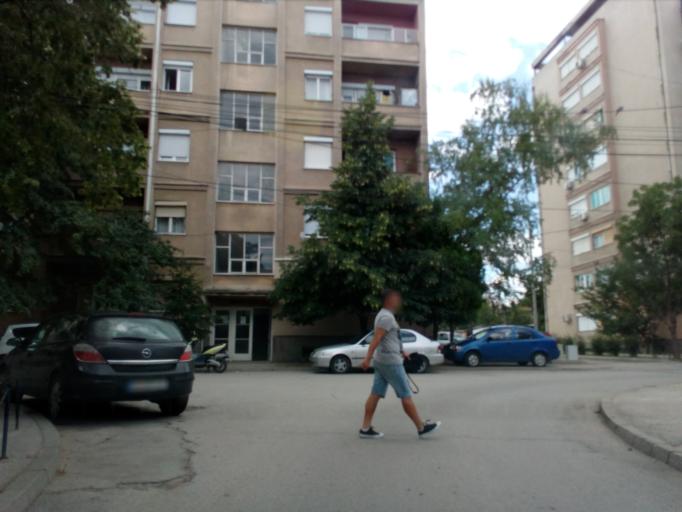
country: MK
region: Veles
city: Veles
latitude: 41.7179
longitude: 21.7697
